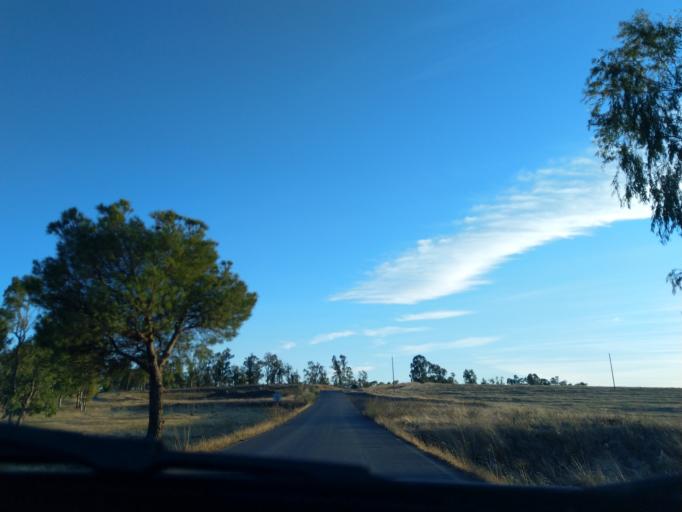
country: ES
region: Extremadura
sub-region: Provincia de Badajoz
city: Berlanga
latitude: 38.2740
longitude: -5.8208
